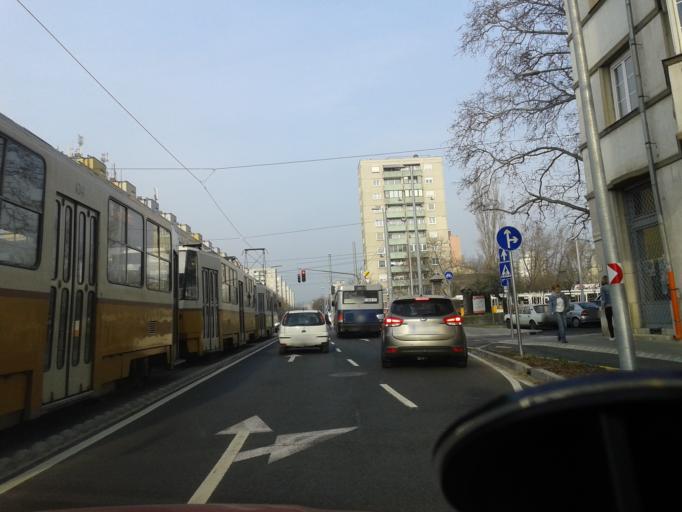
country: HU
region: Budapest
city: Budapest XI. keruelet
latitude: 47.4624
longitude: 19.0433
